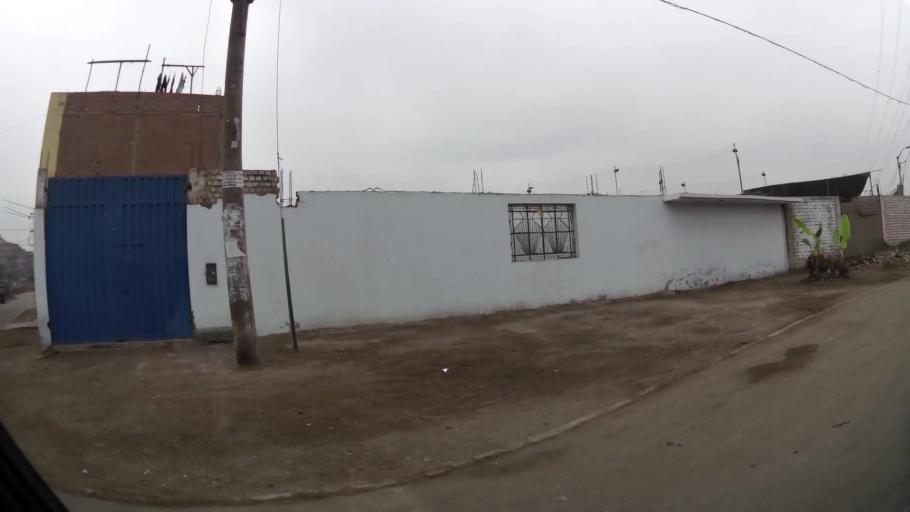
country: PE
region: Lima
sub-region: Lima
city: Urb. Santo Domingo
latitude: -11.8751
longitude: -77.0666
